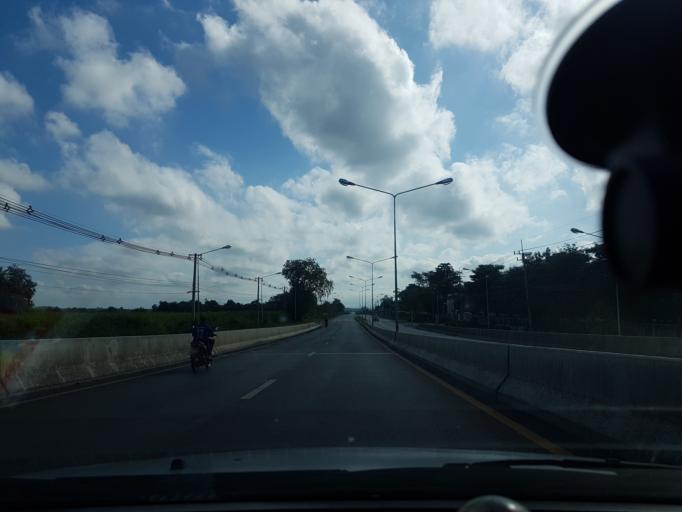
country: TH
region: Lop Buri
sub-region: Amphoe Tha Luang
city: Tha Luang
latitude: 15.0790
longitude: 101.0183
